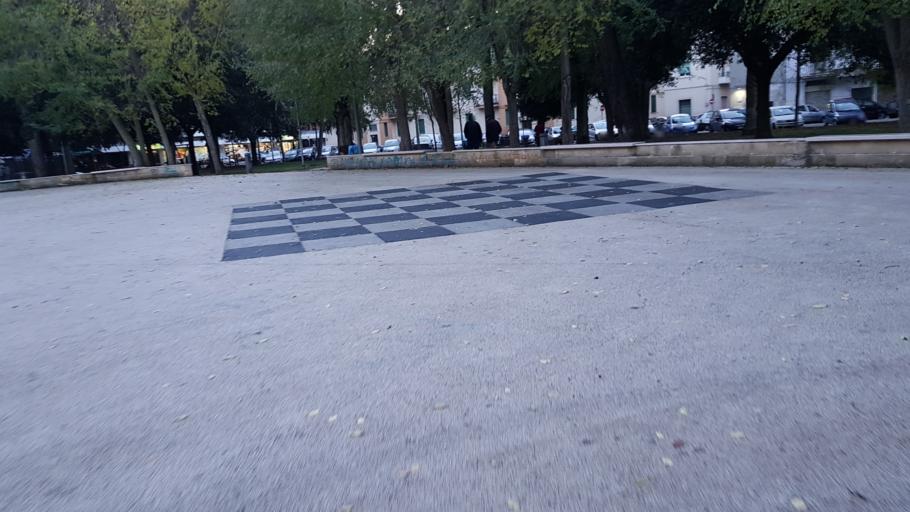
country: IT
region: Apulia
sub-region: Provincia di Bari
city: Gioia del Colle
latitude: 40.7959
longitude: 16.9225
